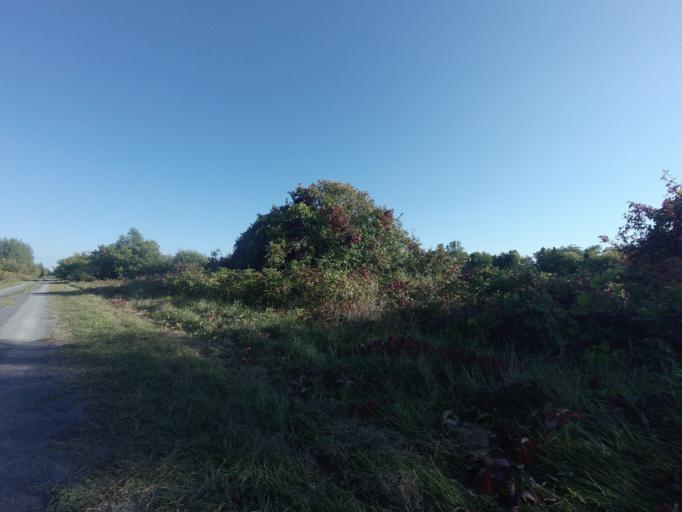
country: CA
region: Ontario
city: Hawkesbury
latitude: 45.5178
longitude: -74.5233
